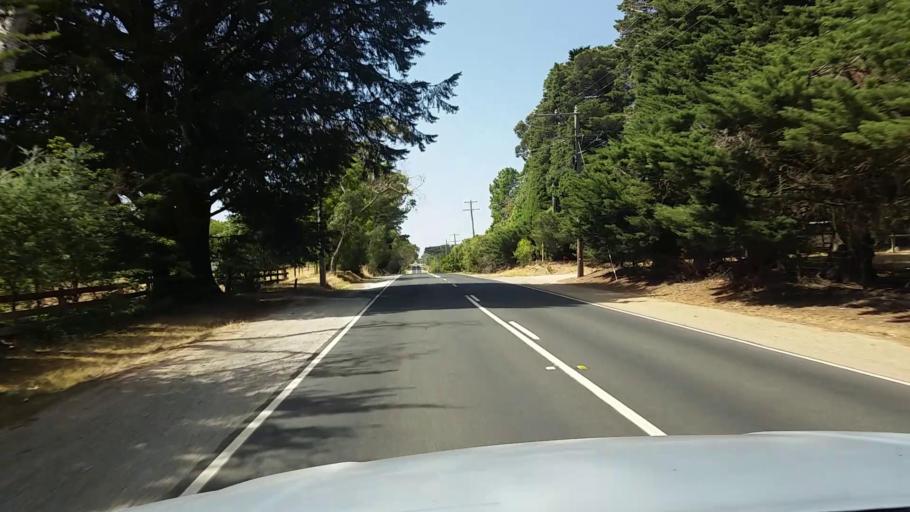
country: AU
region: Victoria
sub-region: Mornington Peninsula
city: Moorooduc
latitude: -38.2572
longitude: 145.1369
